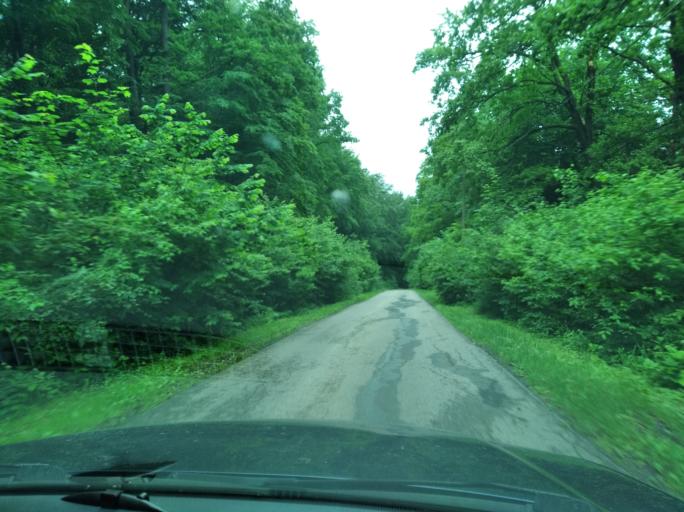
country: PL
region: Subcarpathian Voivodeship
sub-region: Powiat jaroslawski
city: Pruchnik
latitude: 49.8941
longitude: 22.5244
